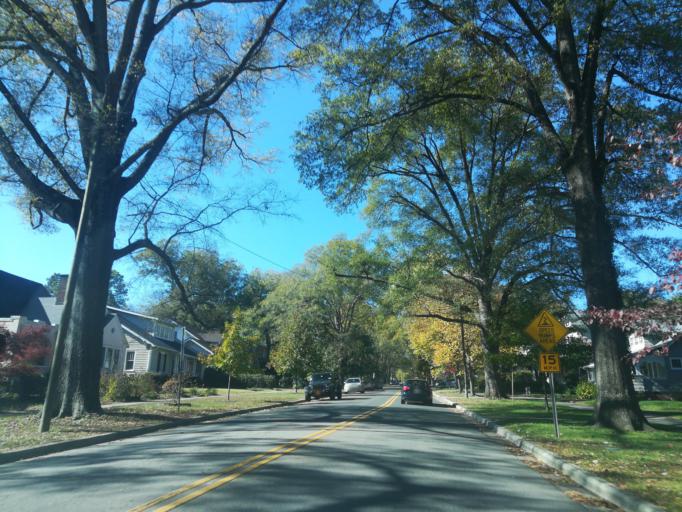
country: US
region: North Carolina
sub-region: Durham County
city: Durham
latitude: 36.0056
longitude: -78.9083
